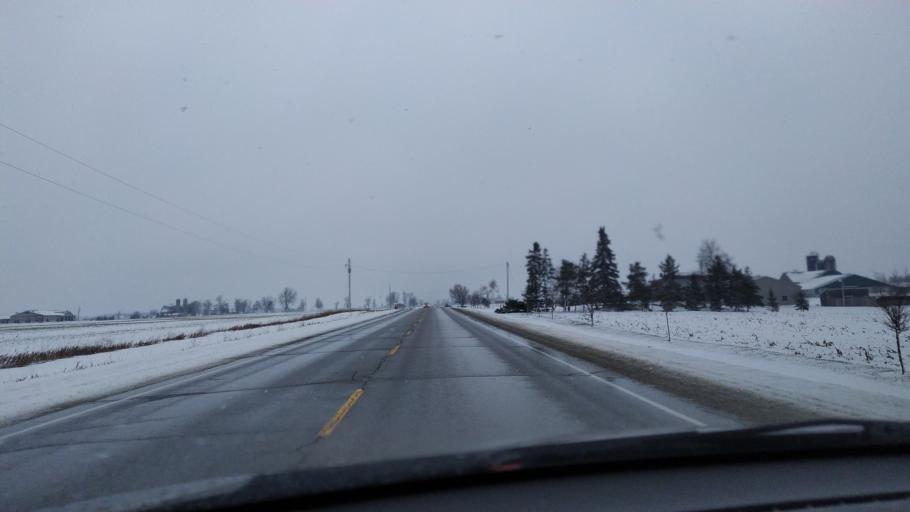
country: CA
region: Ontario
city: Stratford
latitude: 43.5397
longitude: -80.8643
